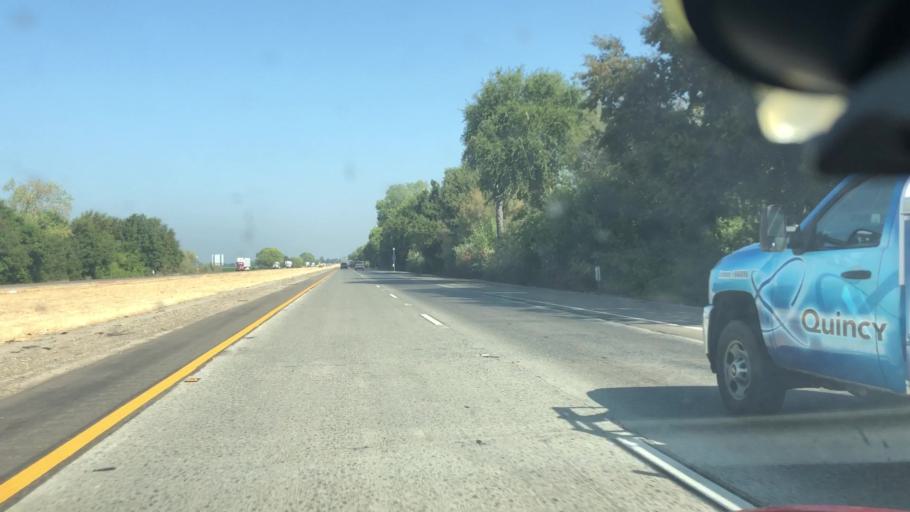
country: US
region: California
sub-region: San Joaquin County
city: Thornton
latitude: 38.2305
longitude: -121.4338
